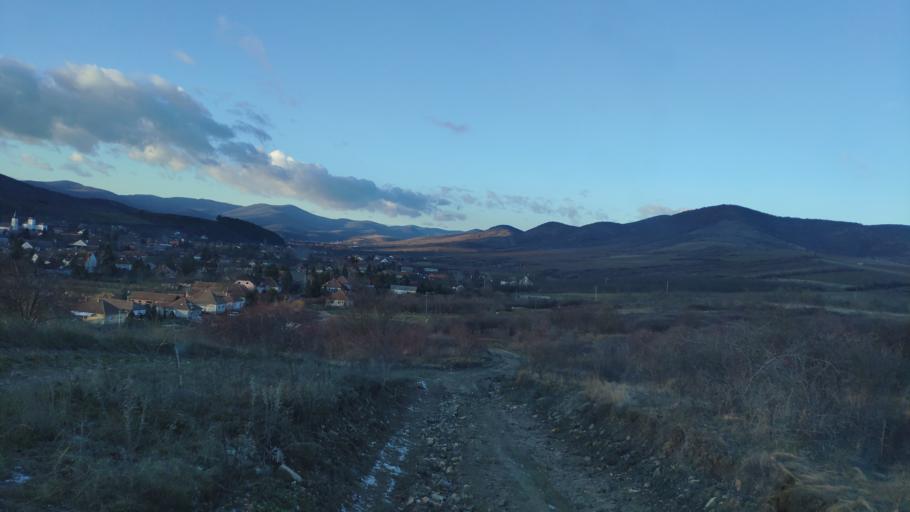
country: HU
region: Borsod-Abauj-Zemplen
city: Tolcsva
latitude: 48.2795
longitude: 21.4584
